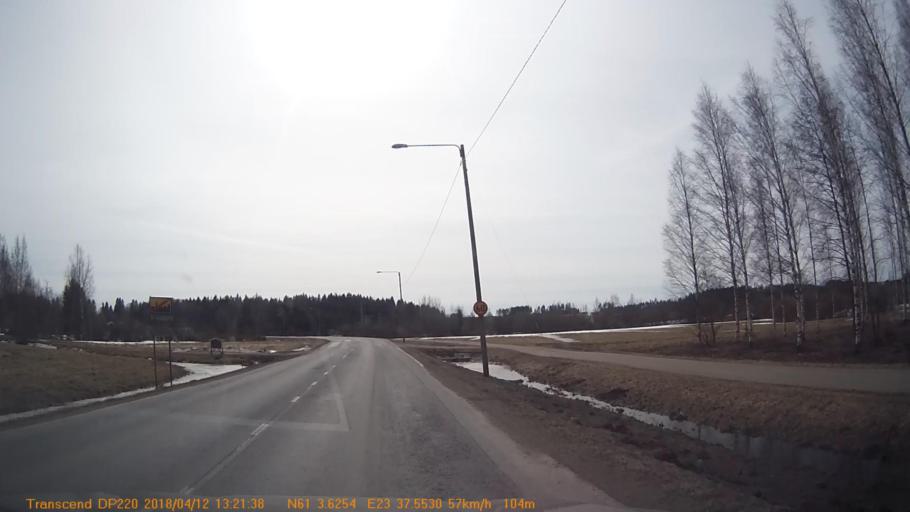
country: FI
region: Pirkanmaa
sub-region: Etelae-Pirkanmaa
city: Urjala
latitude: 61.0596
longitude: 23.6253
